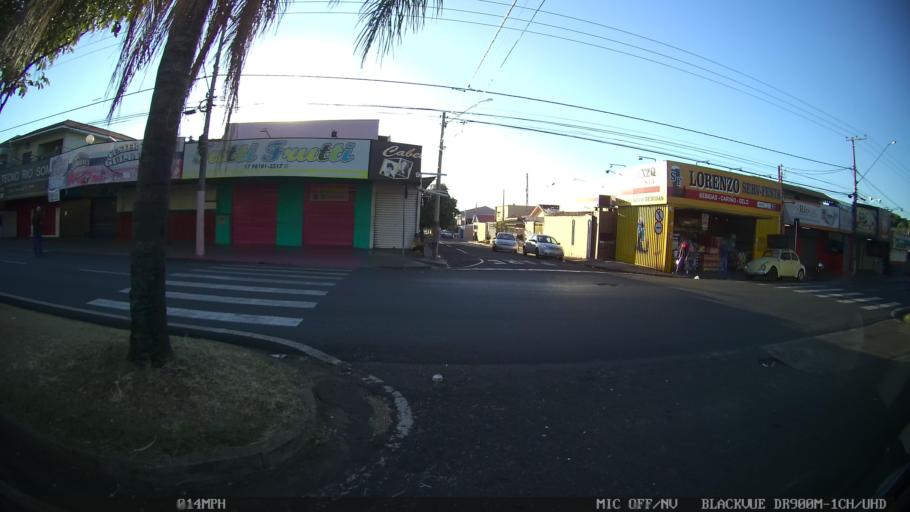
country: BR
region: Sao Paulo
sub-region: Sao Jose Do Rio Preto
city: Sao Jose do Rio Preto
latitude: -20.7748
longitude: -49.3651
